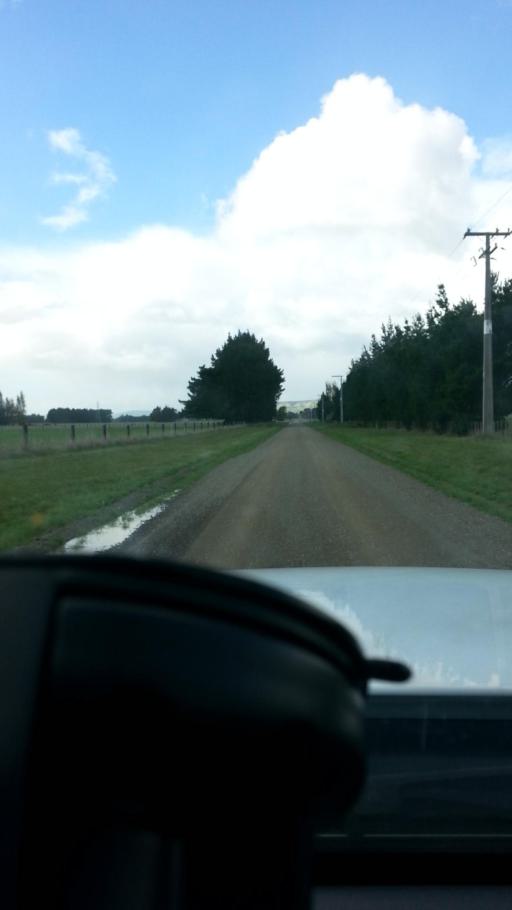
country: NZ
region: Wellington
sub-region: Masterton District
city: Masterton
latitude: -41.1189
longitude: 175.4092
